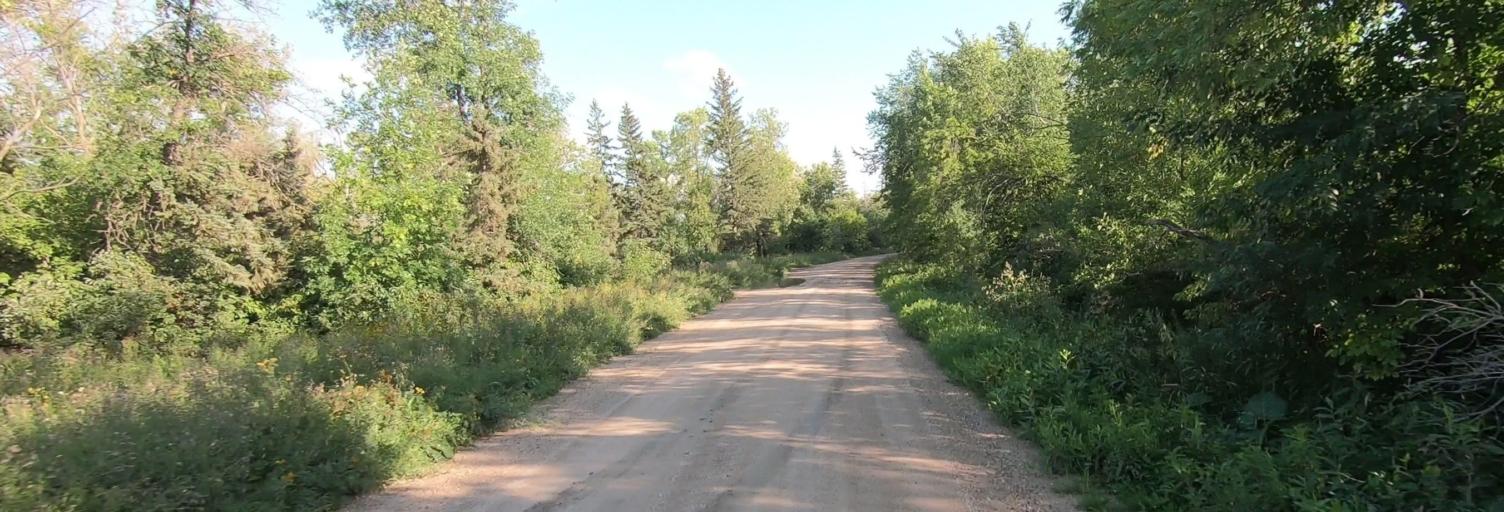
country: CA
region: Manitoba
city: Selkirk
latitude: 50.2761
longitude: -96.8510
